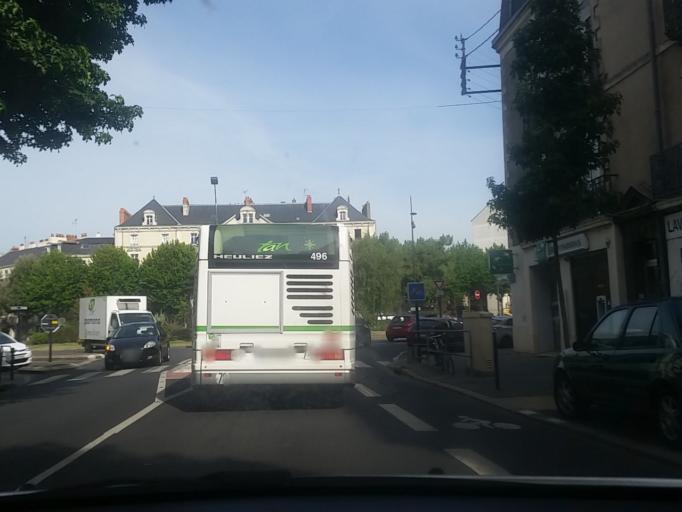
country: FR
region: Pays de la Loire
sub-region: Departement de la Loire-Atlantique
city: Nantes
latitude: 47.2050
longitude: -1.5538
